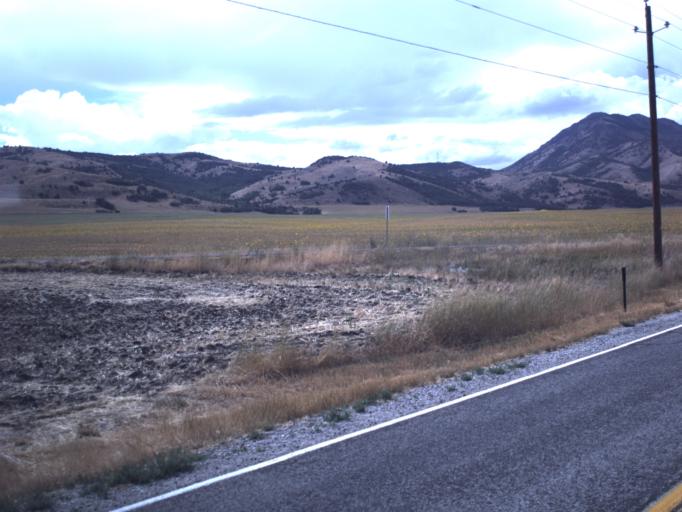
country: US
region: Utah
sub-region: Cache County
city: Benson
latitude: 41.8865
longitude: -112.0344
